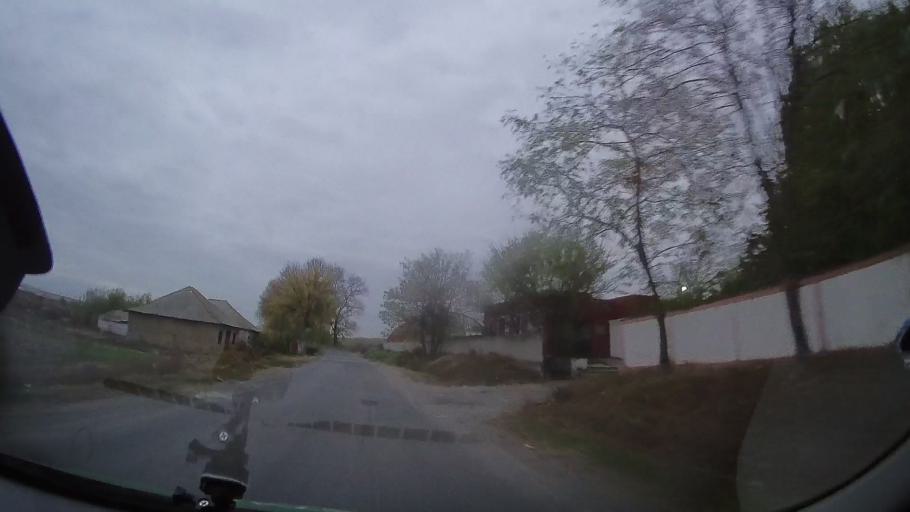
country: RO
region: Tulcea
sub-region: Comuna Mihai Bravu
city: Turda
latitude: 44.9677
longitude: 28.6303
